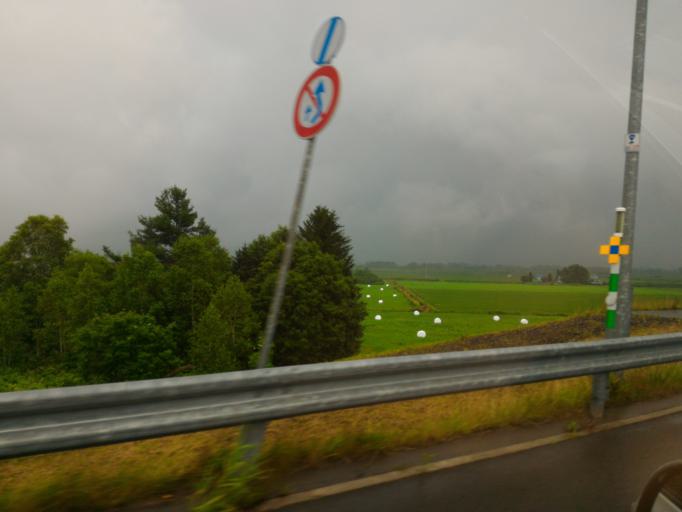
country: JP
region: Hokkaido
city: Nayoro
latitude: 44.3760
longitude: 142.4295
